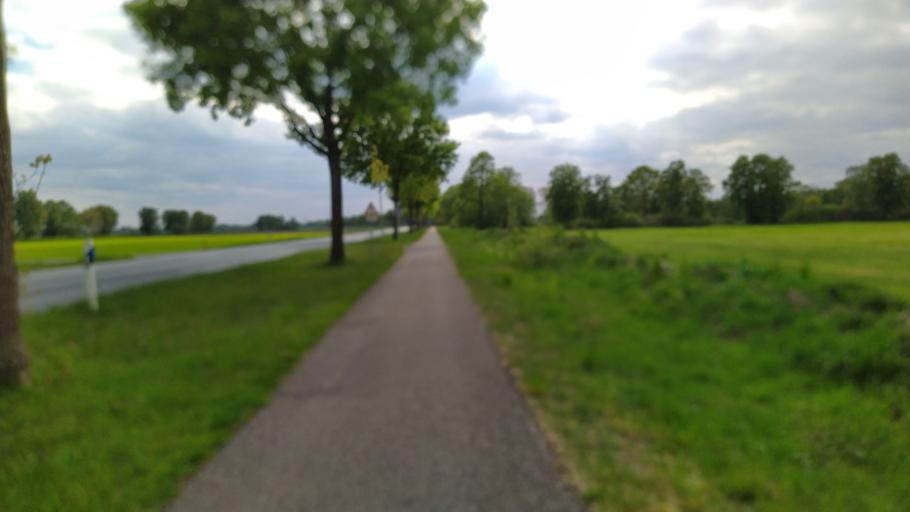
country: DE
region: Lower Saxony
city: Tarmstedt
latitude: 53.2117
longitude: 9.0461
